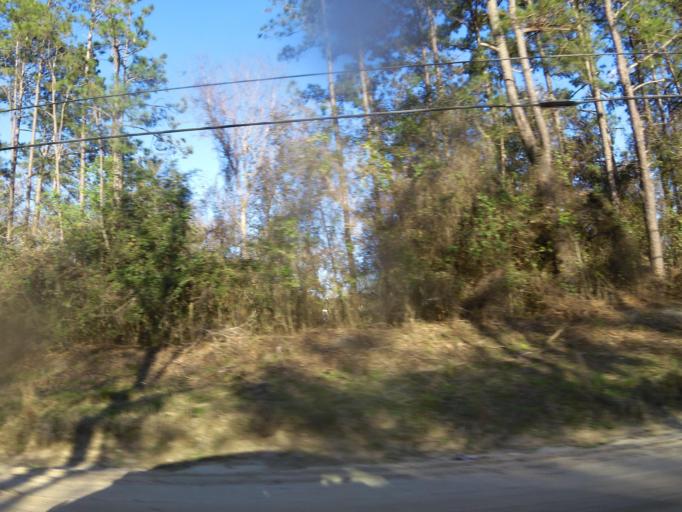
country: US
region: Florida
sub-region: Clay County
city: Middleburg
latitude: 30.1249
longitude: -81.8818
